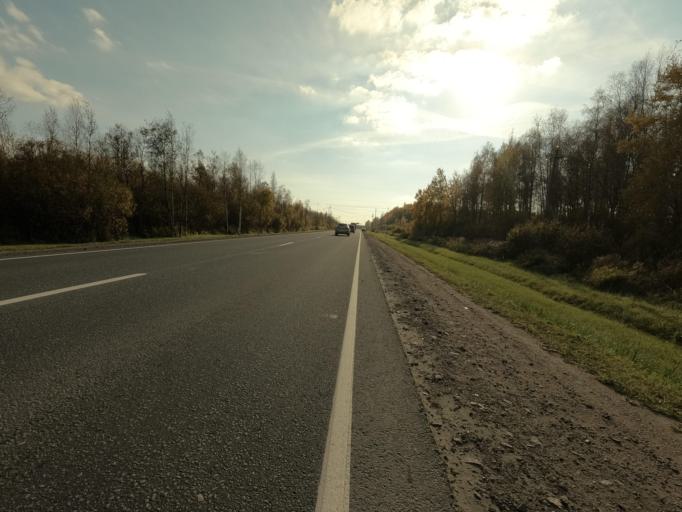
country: RU
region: Leningrad
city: Mga
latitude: 59.7652
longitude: 31.0956
